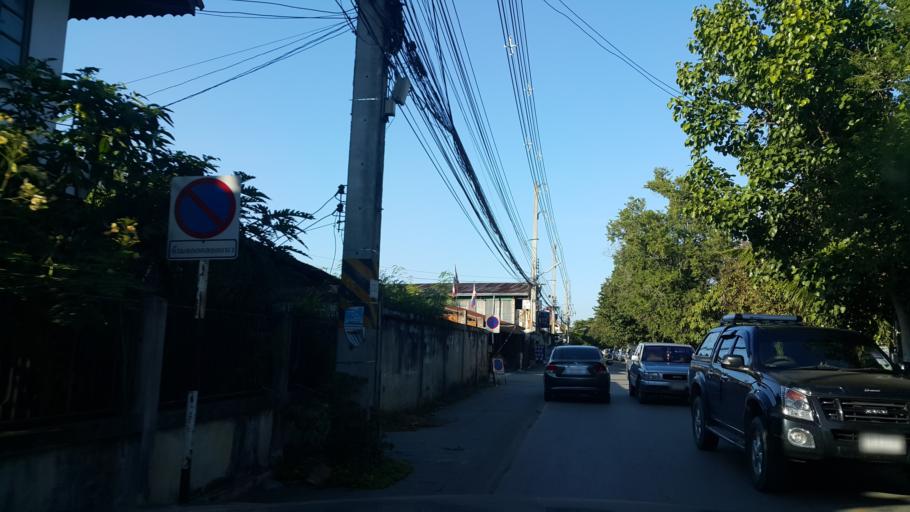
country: TH
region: Lamphun
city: Lamphun
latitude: 18.5749
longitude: 99.0033
